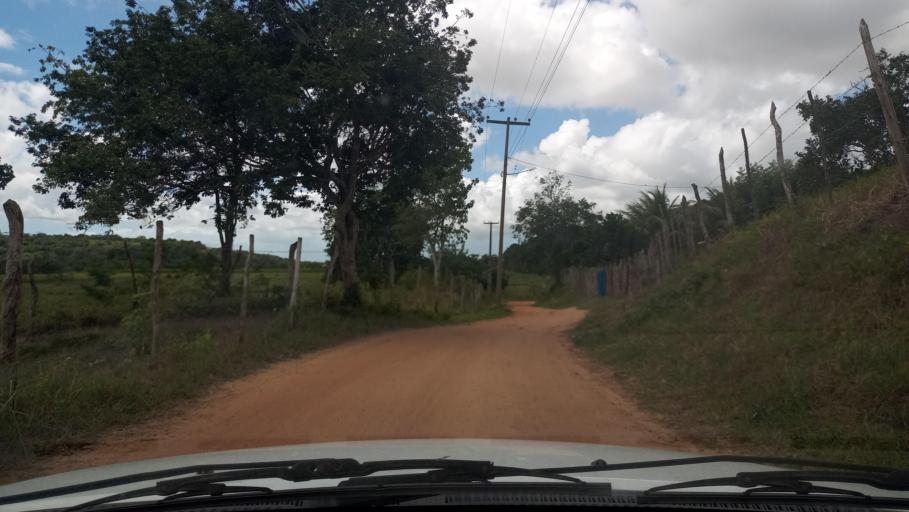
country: BR
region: Rio Grande do Norte
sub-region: Goianinha
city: Goianinha
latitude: -6.2605
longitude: -35.2510
